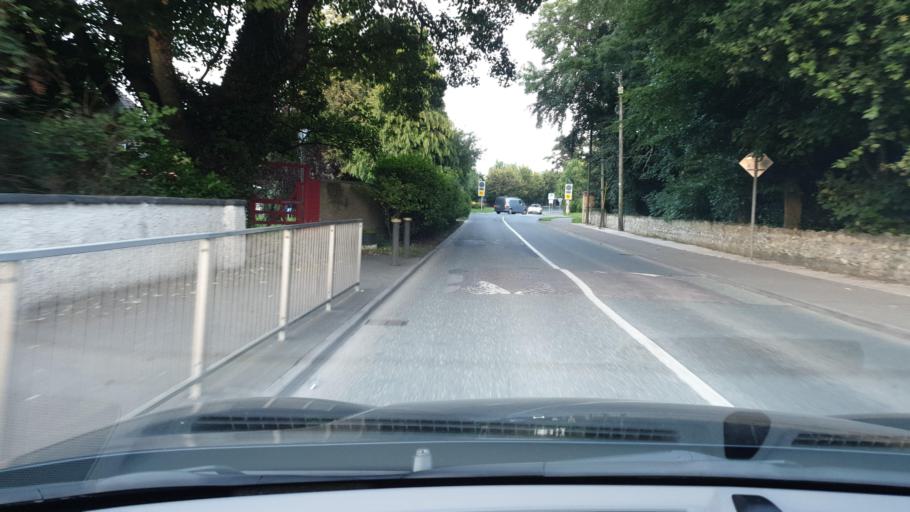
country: IE
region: Leinster
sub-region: Kildare
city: Kill
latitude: 53.2502
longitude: -6.5866
